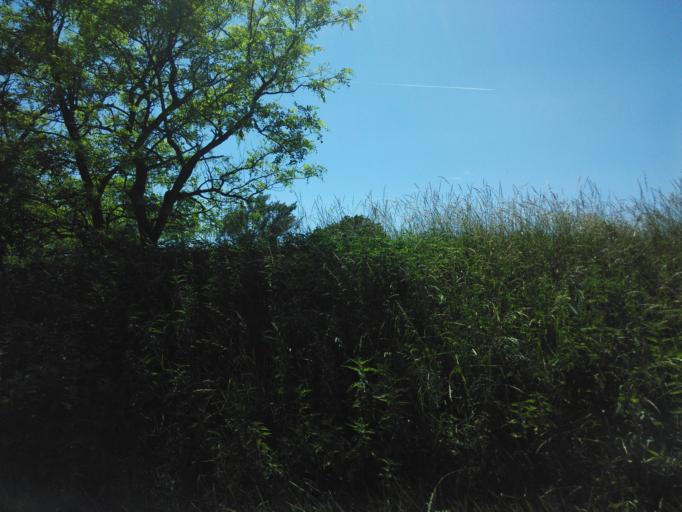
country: HU
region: Fejer
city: Bodajk
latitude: 47.3506
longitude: 18.2248
